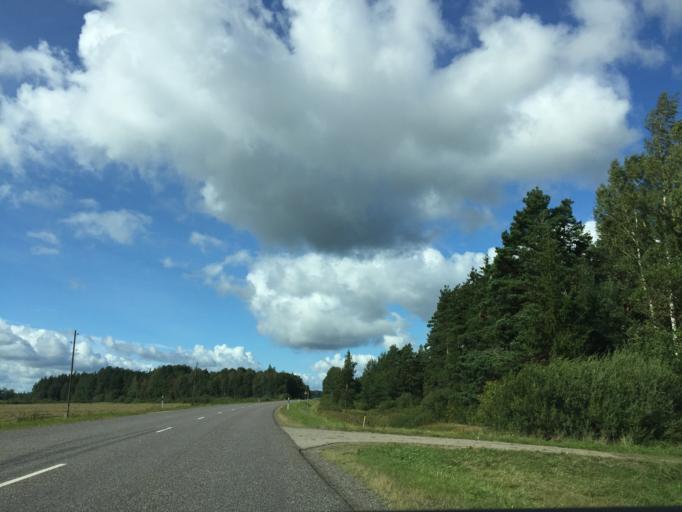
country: LV
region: Kuldigas Rajons
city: Kuldiga
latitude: 56.9952
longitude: 22.1191
